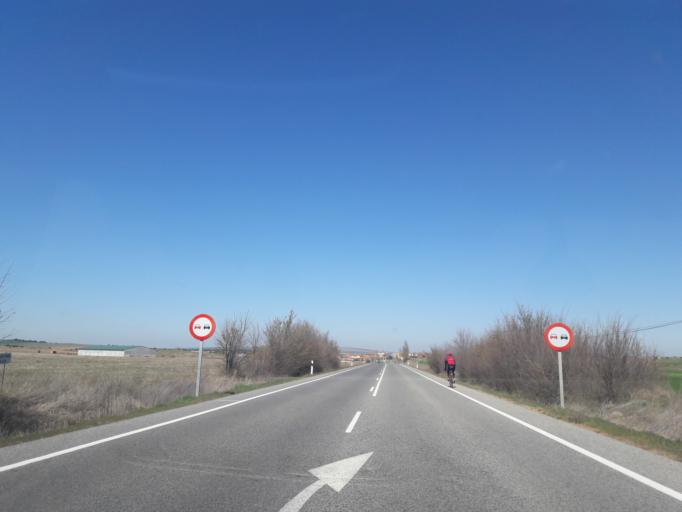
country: ES
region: Castille and Leon
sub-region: Provincia de Salamanca
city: Mozarbez
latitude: 40.8494
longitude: -5.6455
